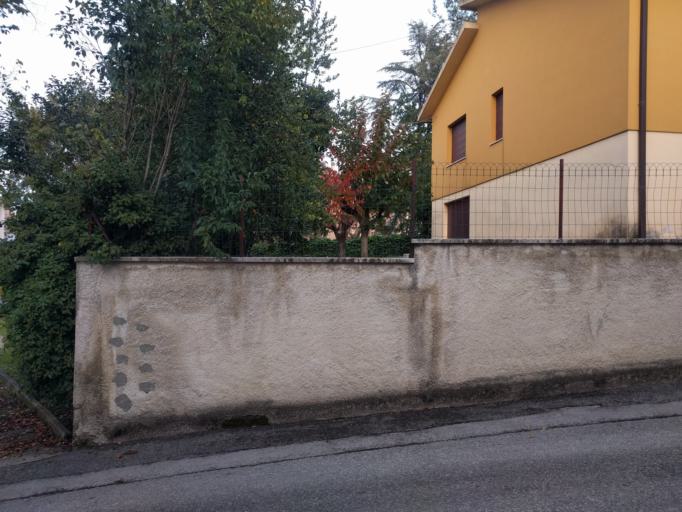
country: IT
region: The Marches
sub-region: Provincia di Ancona
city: Ostra
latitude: 43.6114
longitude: 13.1537
